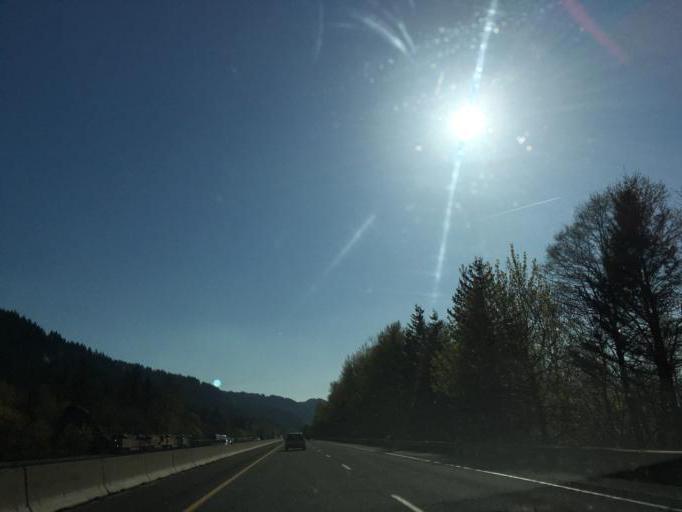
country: US
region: Washington
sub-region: Clark County
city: Washougal
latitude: 45.5673
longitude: -122.1655
